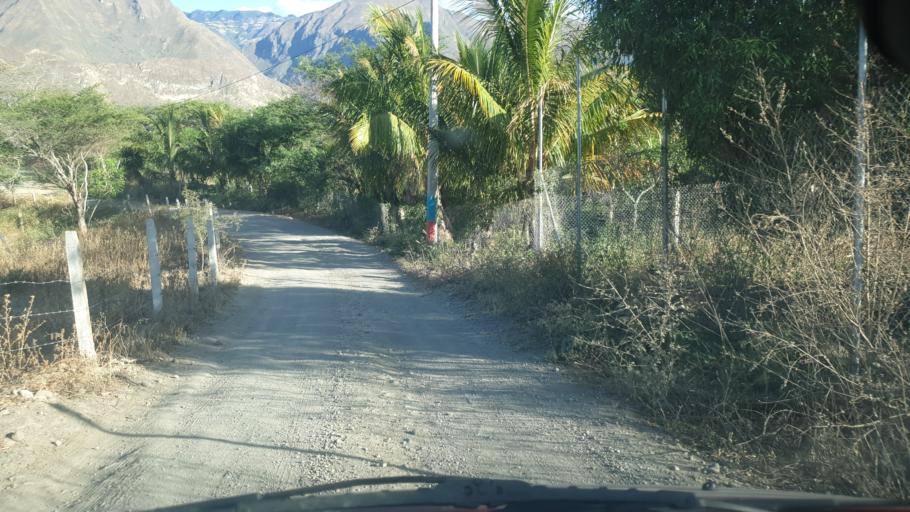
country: EC
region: Azuay
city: Cuenca
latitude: -3.2922
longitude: -79.2858
